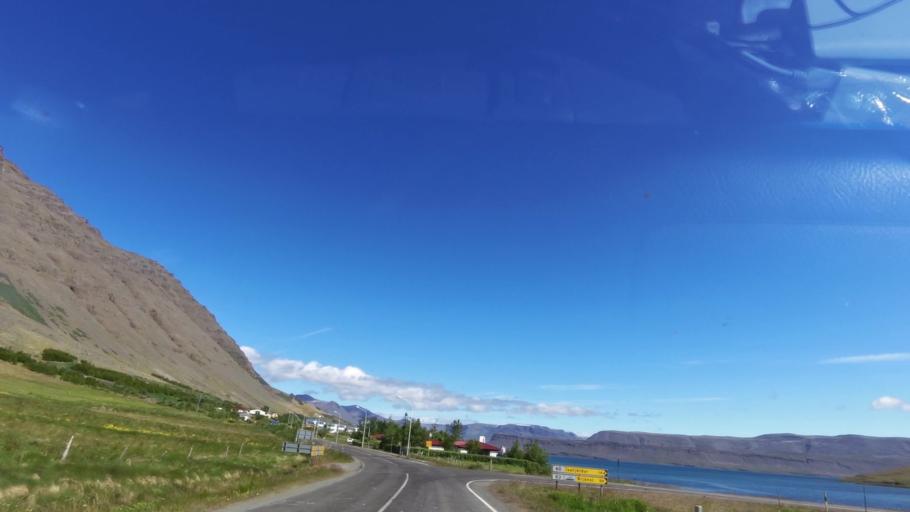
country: IS
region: Westfjords
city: Isafjoerdur
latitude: 65.6768
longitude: -23.6135
